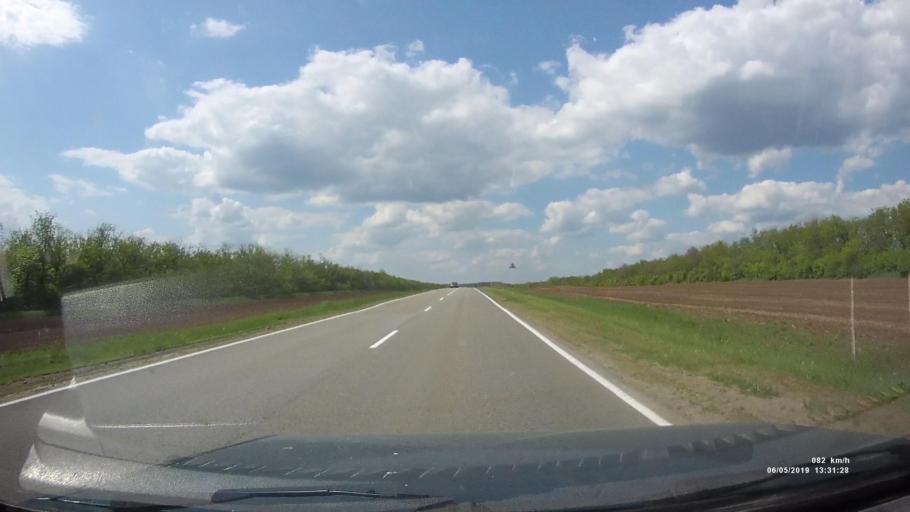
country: RU
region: Rostov
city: Ust'-Donetskiy
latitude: 47.6769
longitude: 40.8102
